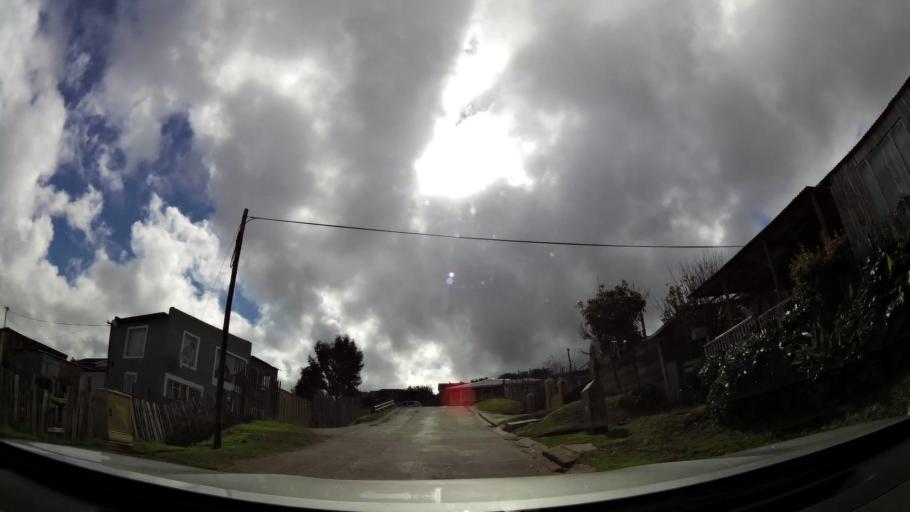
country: ZA
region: Western Cape
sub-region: Eden District Municipality
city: Knysna
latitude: -34.0519
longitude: 23.0998
